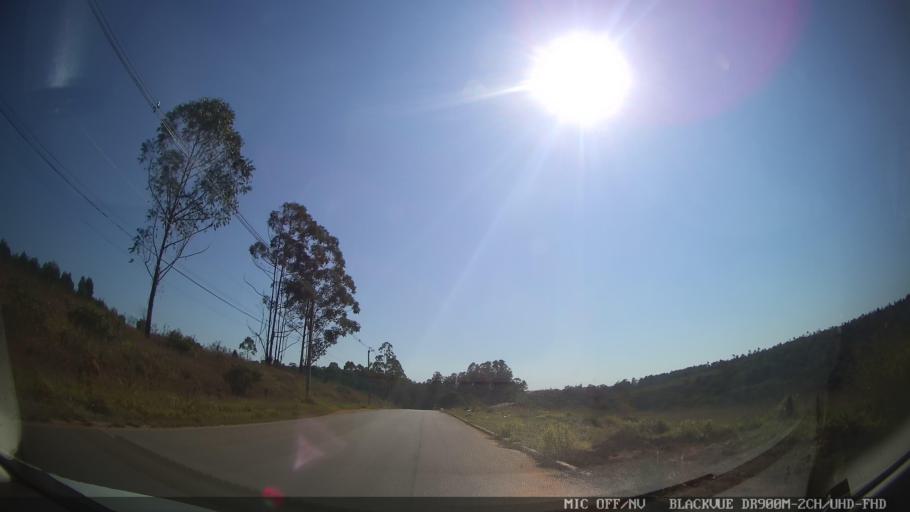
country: BR
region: Sao Paulo
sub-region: Itupeva
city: Itupeva
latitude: -23.1301
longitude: -47.0452
